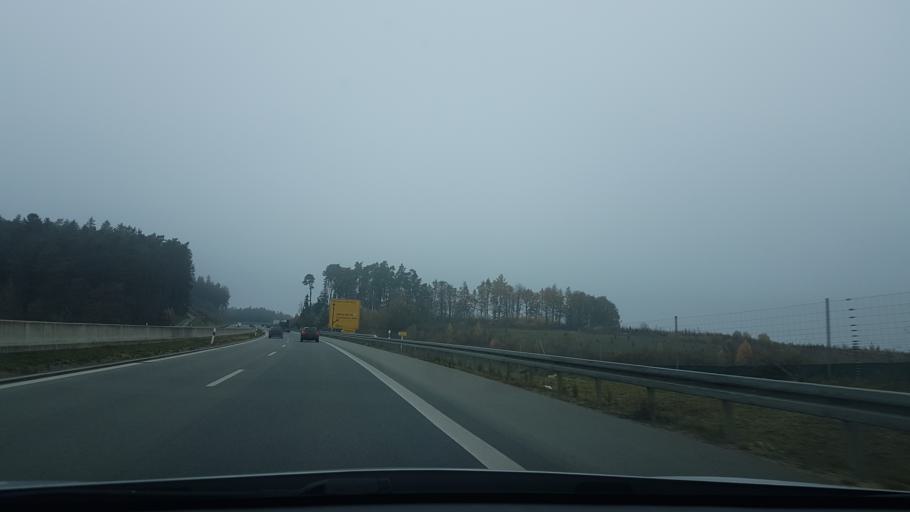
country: DE
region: Bavaria
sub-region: Lower Bavaria
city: Ergoldsbach
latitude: 48.7080
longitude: 12.1757
